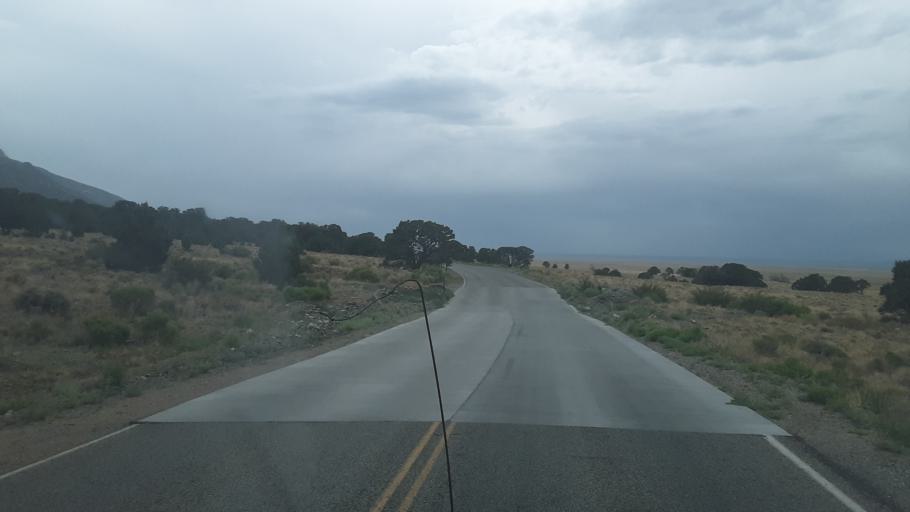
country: US
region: Colorado
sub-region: Custer County
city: Westcliffe
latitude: 37.7294
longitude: -105.5156
